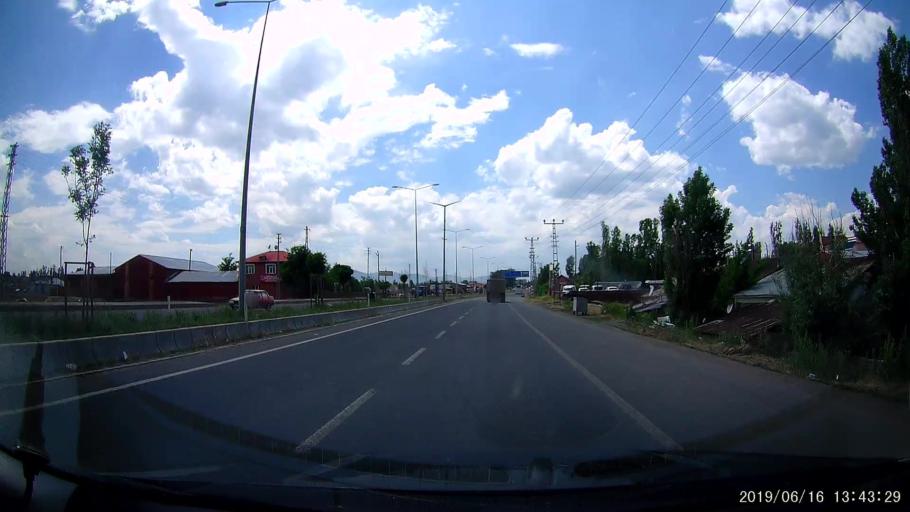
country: TR
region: Agri
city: Agri
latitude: 39.7080
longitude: 43.0545
